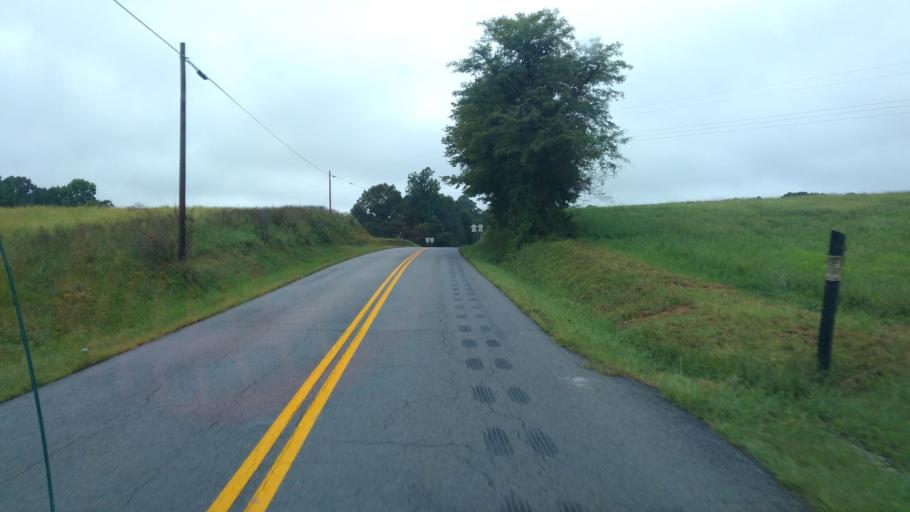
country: US
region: Kentucky
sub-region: Fleming County
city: Flemingsburg
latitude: 38.4156
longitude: -83.5599
